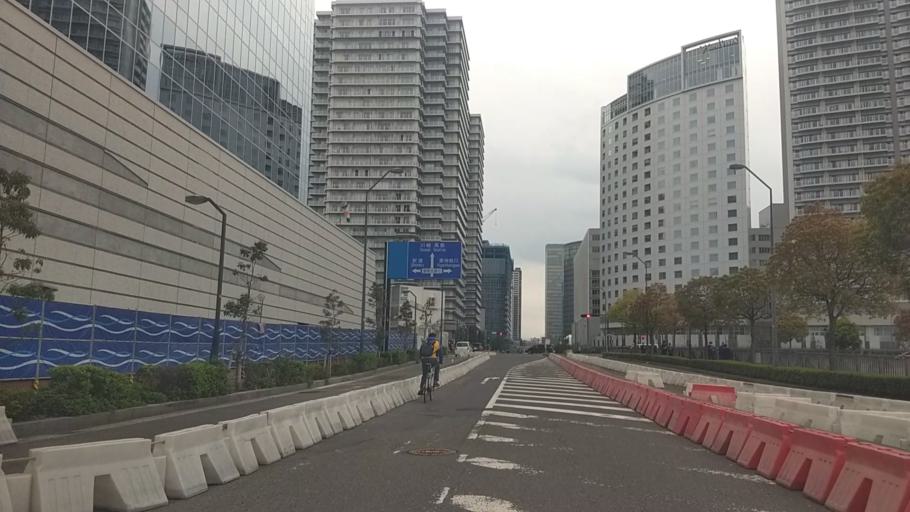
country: JP
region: Kanagawa
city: Yokohama
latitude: 35.4627
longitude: 139.6347
